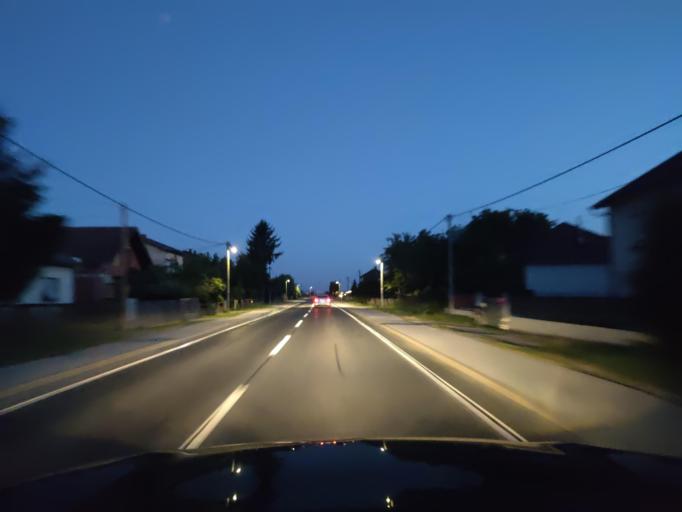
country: HR
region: Medimurska
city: Mackovec
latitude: 46.4253
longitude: 16.4288
